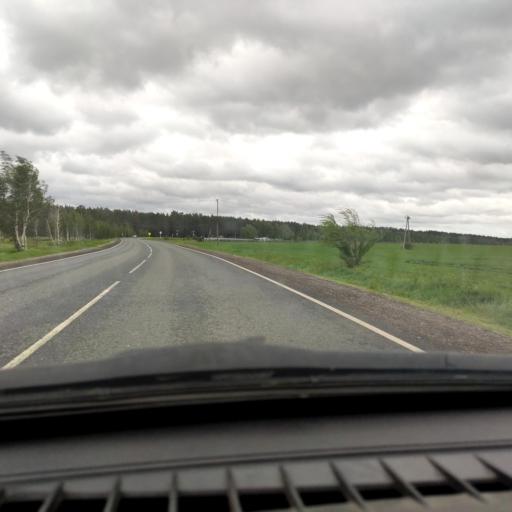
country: RU
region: Samara
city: Povolzhskiy
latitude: 53.6346
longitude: 49.6586
